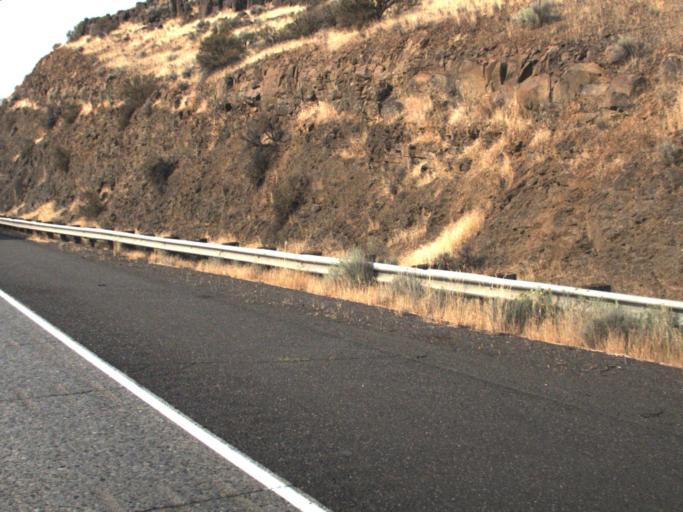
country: US
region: Washington
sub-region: Kittitas County
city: Kittitas
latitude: 46.8088
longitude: -120.3564
